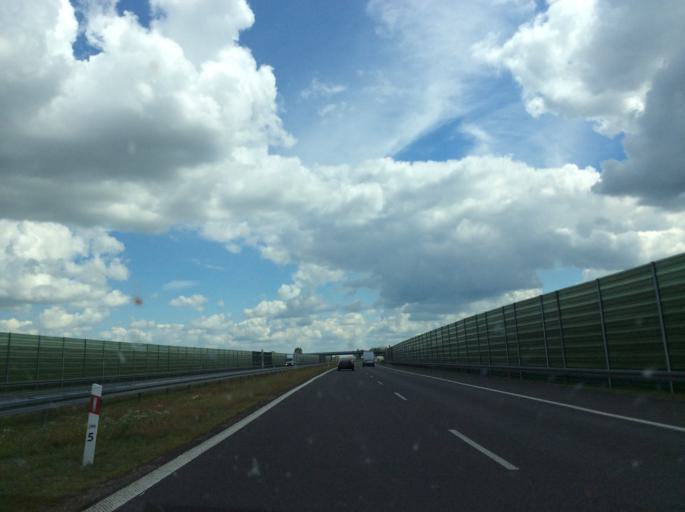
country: PL
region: Greater Poland Voivodeship
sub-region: Powiat kolski
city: Grzegorzew
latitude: 52.1146
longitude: 18.7323
